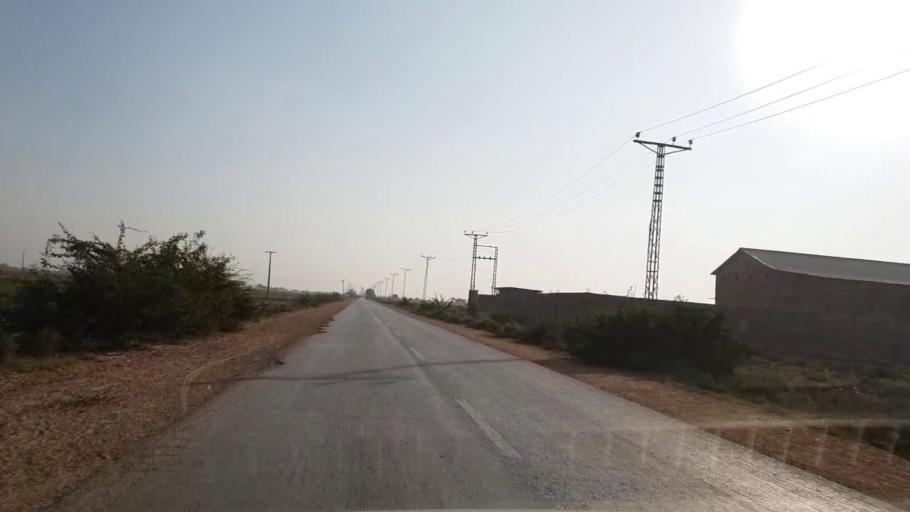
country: PK
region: Sindh
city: Bulri
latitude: 24.8529
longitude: 68.3277
